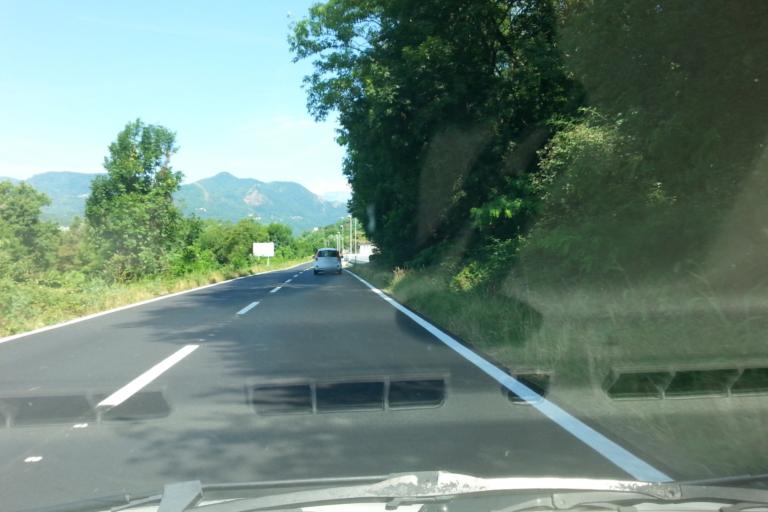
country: IT
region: Piedmont
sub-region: Provincia di Torino
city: Trana
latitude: 45.0472
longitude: 7.4061
